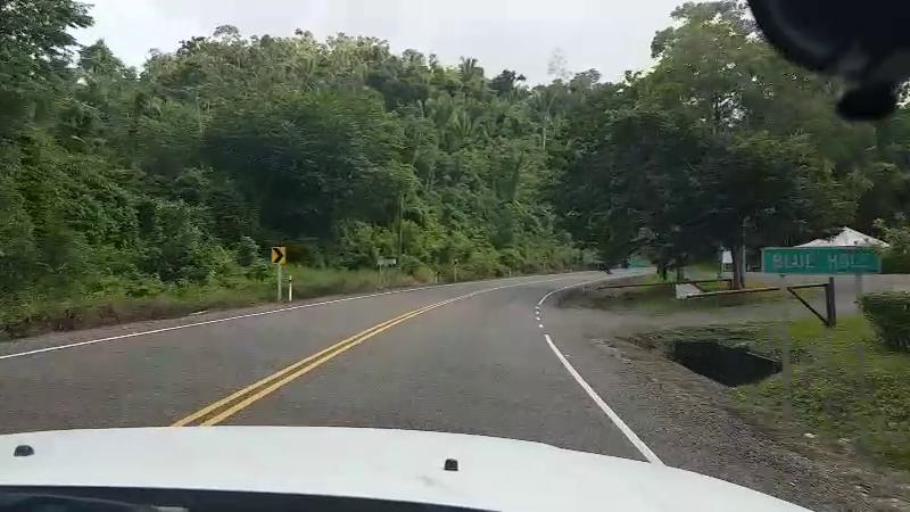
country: BZ
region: Cayo
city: Belmopan
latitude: 17.1586
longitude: -88.6841
